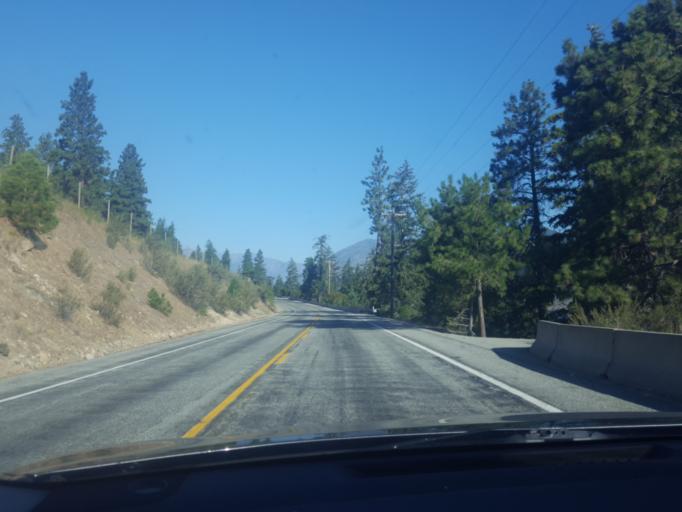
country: US
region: Washington
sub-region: Chelan County
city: Granite Falls
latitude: 47.9867
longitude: -120.2344
